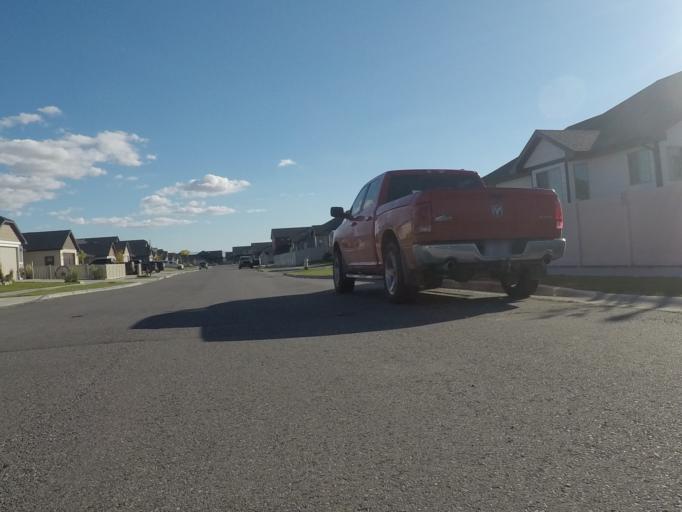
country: US
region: Montana
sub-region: Yellowstone County
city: Laurel
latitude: 45.7826
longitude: -108.6649
